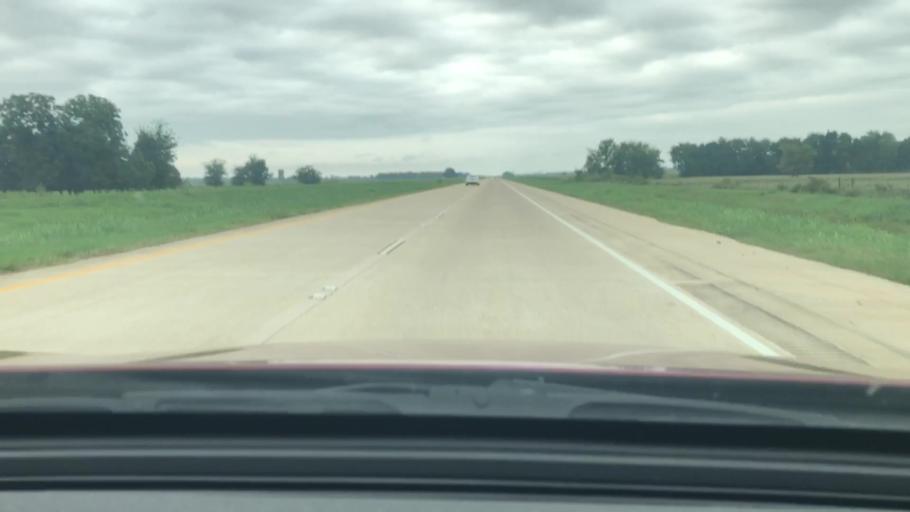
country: US
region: Louisiana
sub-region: Caddo Parish
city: Oil City
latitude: 32.7419
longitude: -93.8784
